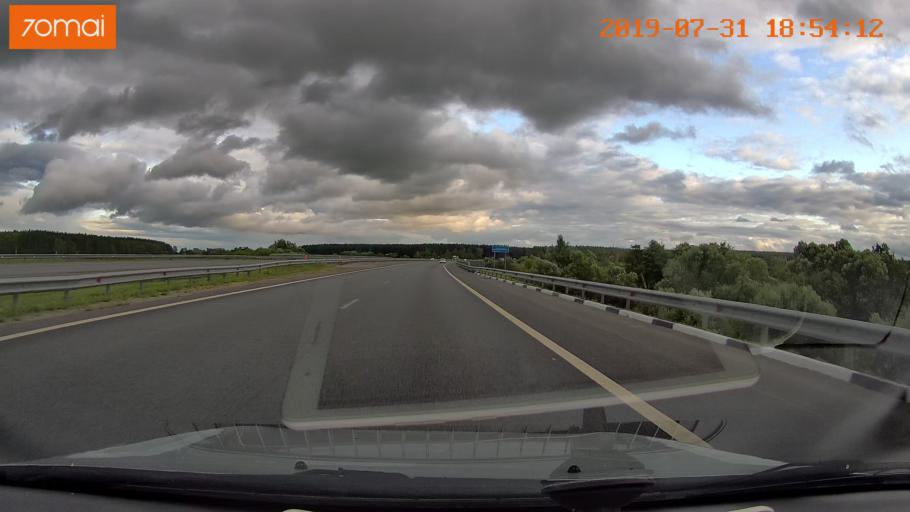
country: RU
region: Moskovskaya
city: Raduzhnyy
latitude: 55.1936
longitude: 38.6672
